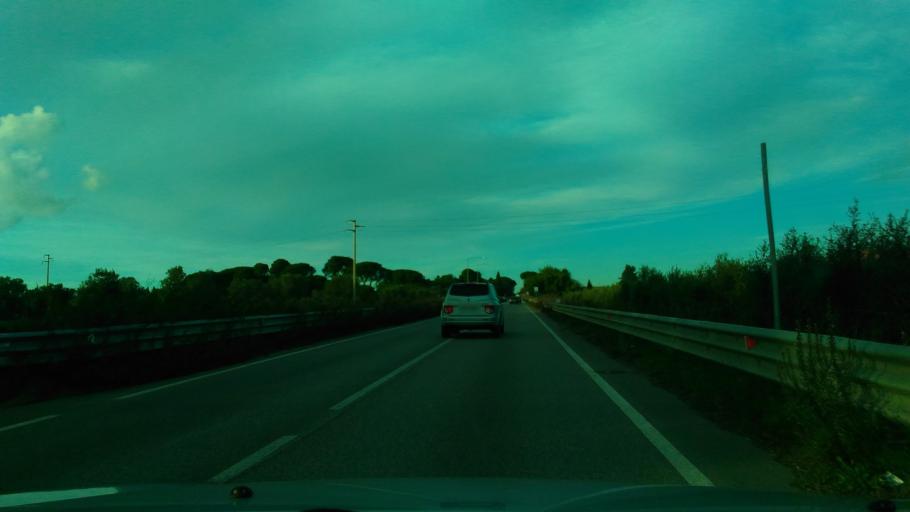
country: IT
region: Tuscany
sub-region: Provincia di Livorno
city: S.P. in Palazzi
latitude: 43.3345
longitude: 10.5060
